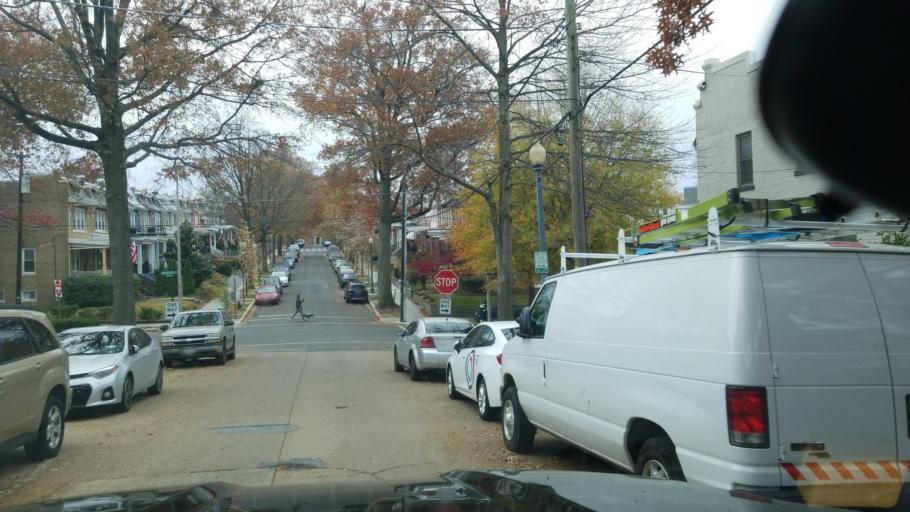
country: US
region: Maryland
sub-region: Prince George's County
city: Chillum
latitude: 38.9447
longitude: -77.0155
